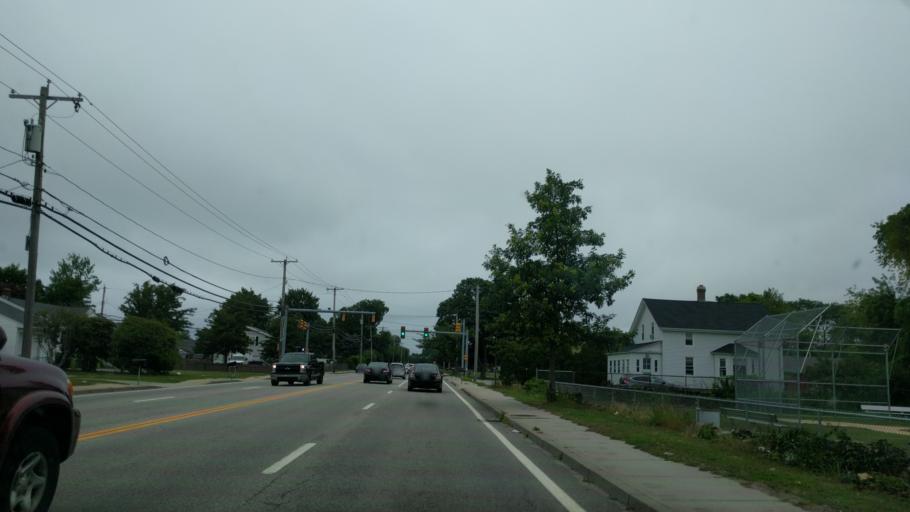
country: US
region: Rhode Island
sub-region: Newport County
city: Middletown
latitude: 41.5400
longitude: -71.2915
